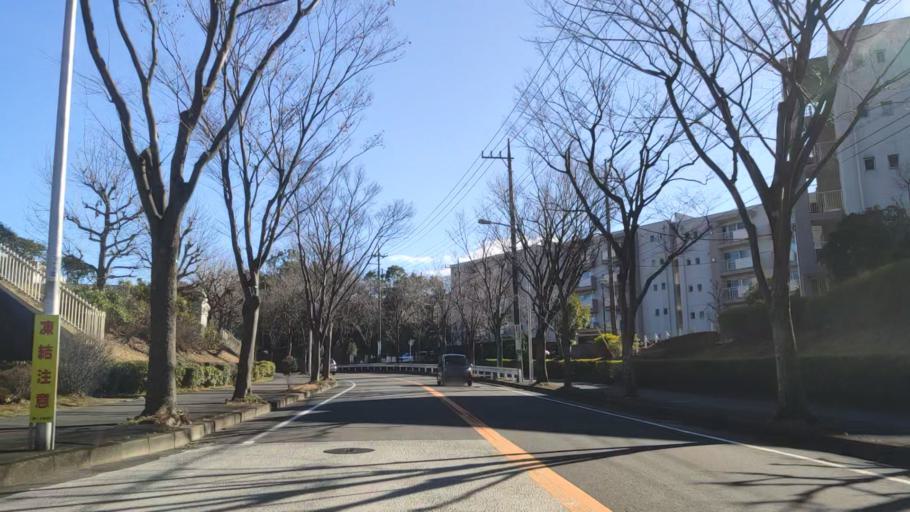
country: JP
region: Tokyo
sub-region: Machida-shi
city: Machida
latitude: 35.5121
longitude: 139.5010
